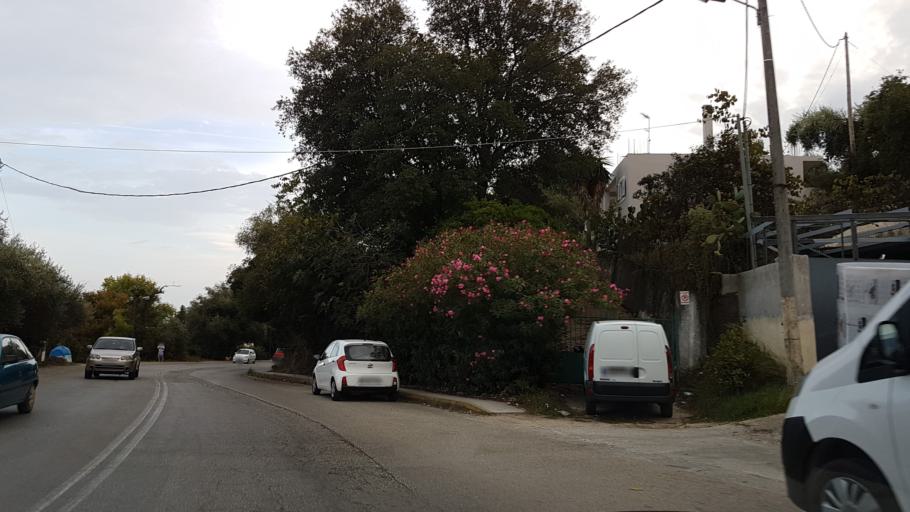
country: GR
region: Ionian Islands
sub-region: Nomos Kerkyras
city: Kontokali
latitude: 39.6842
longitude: 19.8377
